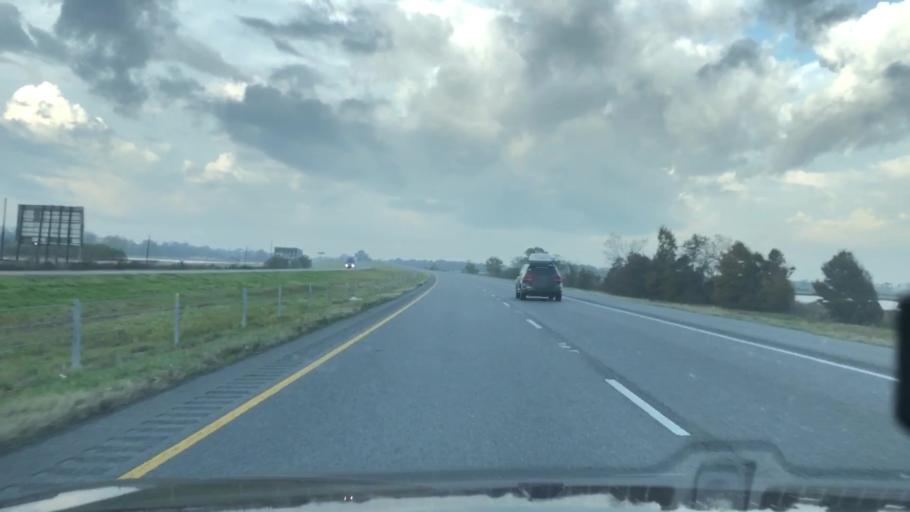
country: US
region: Louisiana
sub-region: Madison Parish
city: Tallulah
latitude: 32.4027
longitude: -91.2186
